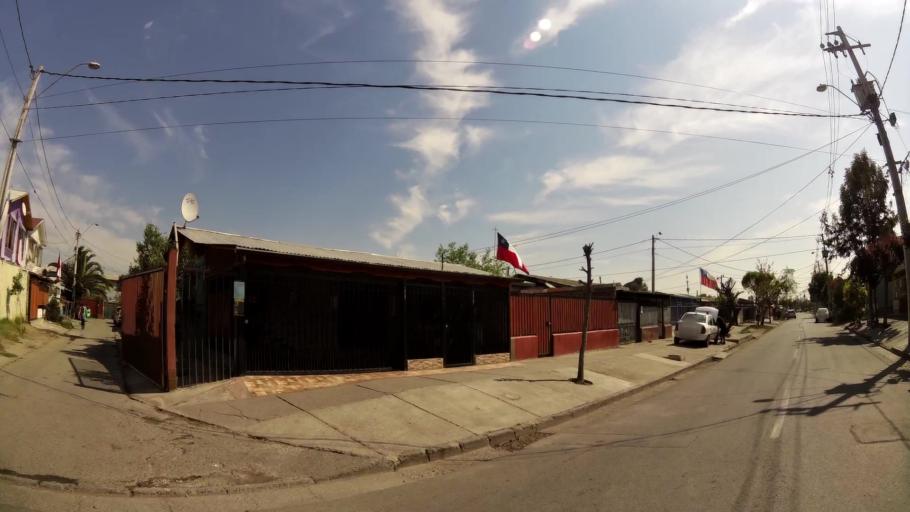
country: CL
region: Santiago Metropolitan
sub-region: Provincia de Santiago
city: La Pintana
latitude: -33.5635
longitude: -70.6449
